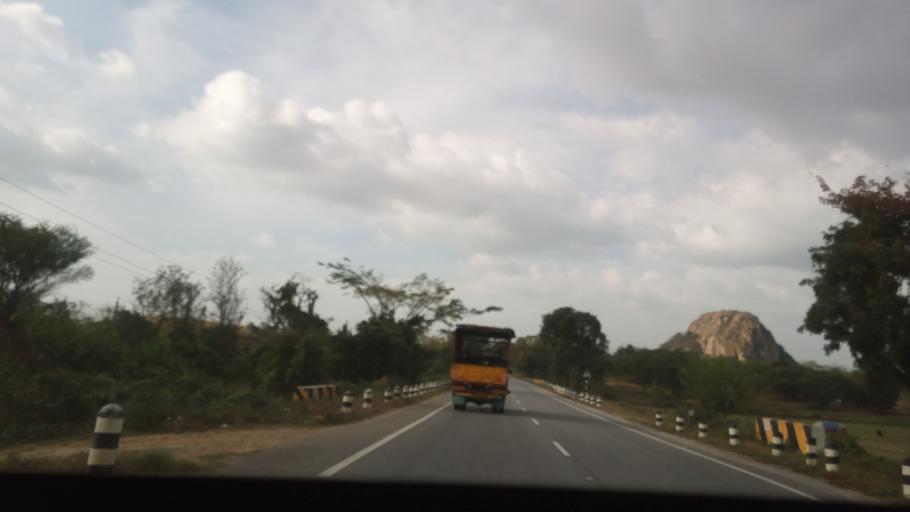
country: IN
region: Karnataka
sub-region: Tumkur
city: Kunigal
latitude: 12.8090
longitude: 77.0371
